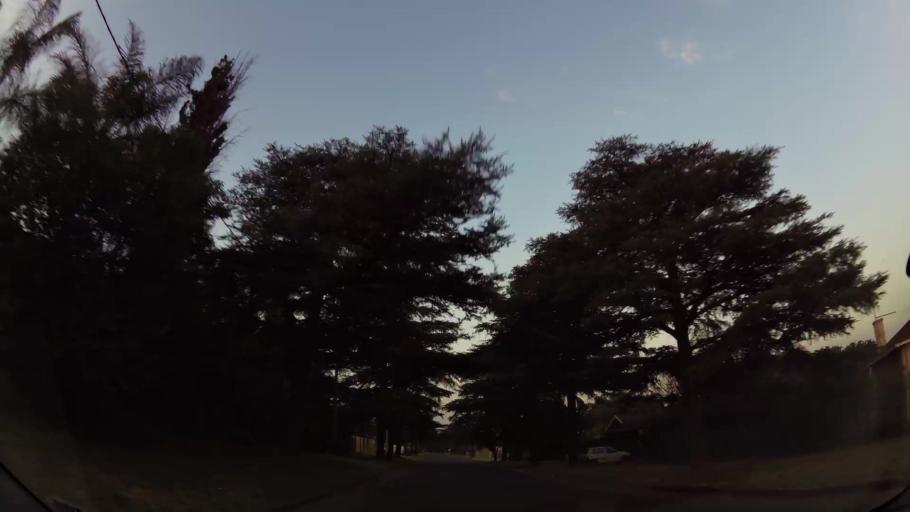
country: ZA
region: Gauteng
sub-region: Ekurhuleni Metropolitan Municipality
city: Benoni
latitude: -26.1783
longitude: 28.3175
